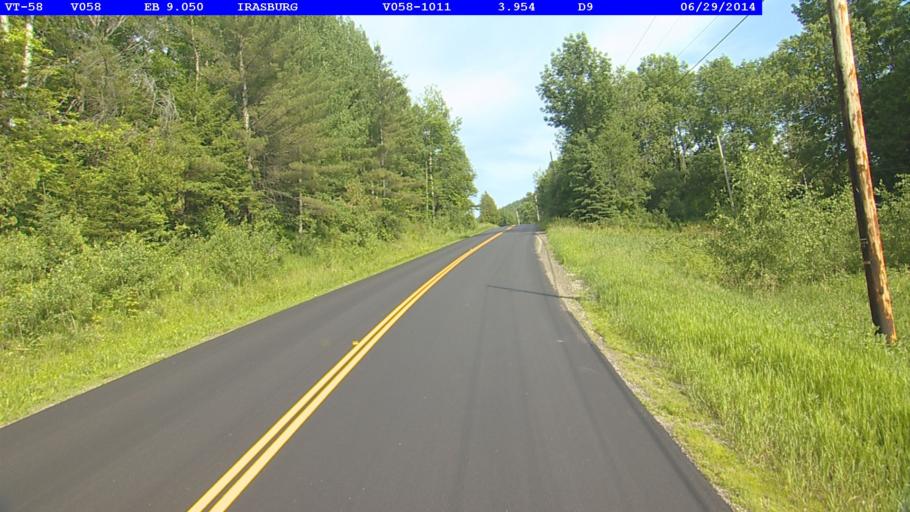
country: US
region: Vermont
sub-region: Orleans County
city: Newport
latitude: 44.8056
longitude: -72.2656
